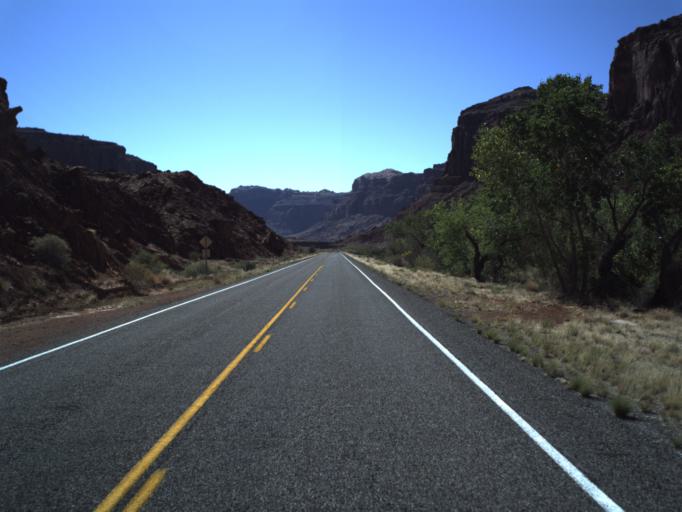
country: US
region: Utah
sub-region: San Juan County
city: Blanding
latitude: 37.9423
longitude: -110.4700
